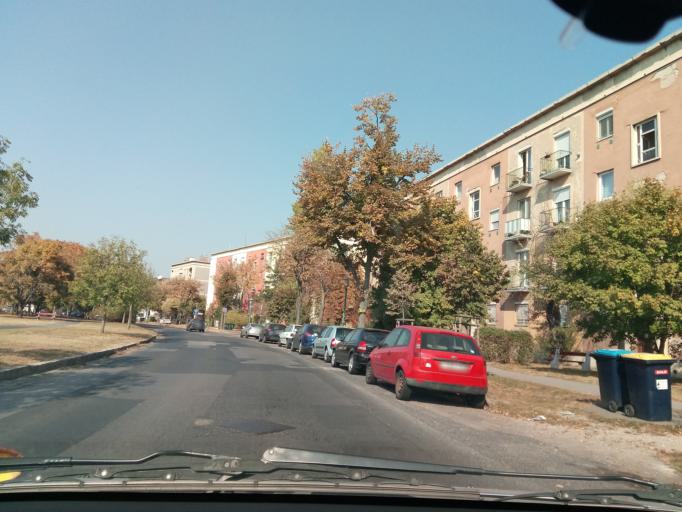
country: HU
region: Budapest
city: Budapest XIV. keruelet
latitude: 47.5047
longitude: 19.1244
